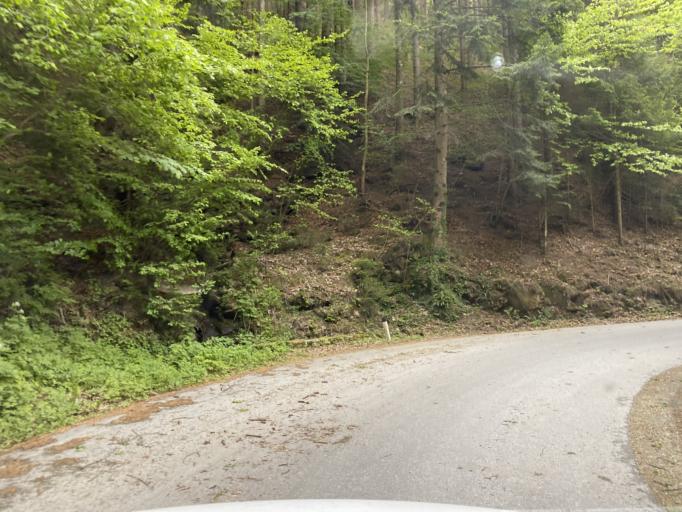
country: AT
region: Styria
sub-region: Politischer Bezirk Weiz
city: Koglhof
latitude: 47.3098
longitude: 15.6981
